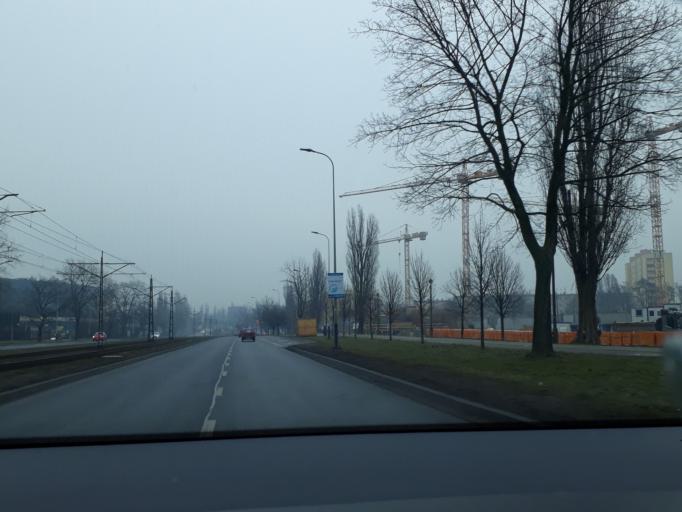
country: PL
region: Lesser Poland Voivodeship
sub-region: Krakow
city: Krakow
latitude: 50.0674
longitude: 20.0066
